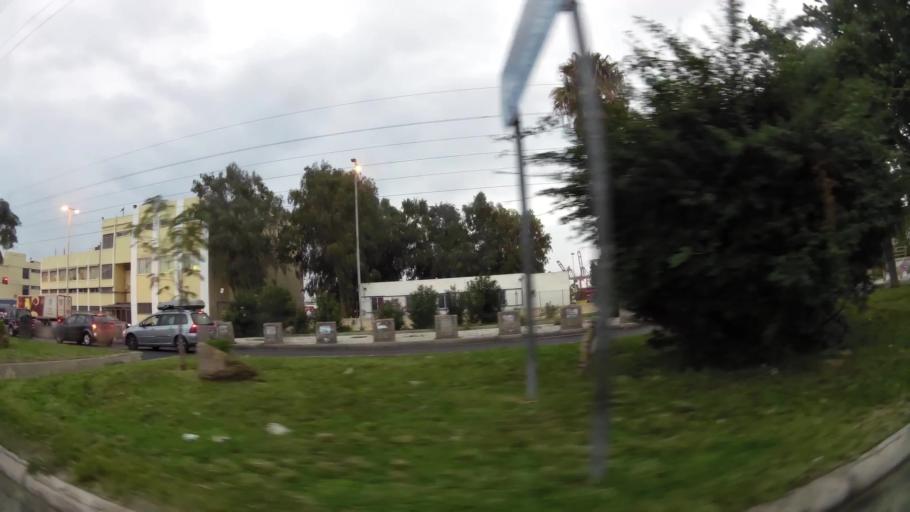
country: GR
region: Attica
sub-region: Nomos Piraios
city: Keratsini
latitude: 37.9592
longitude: 23.6146
